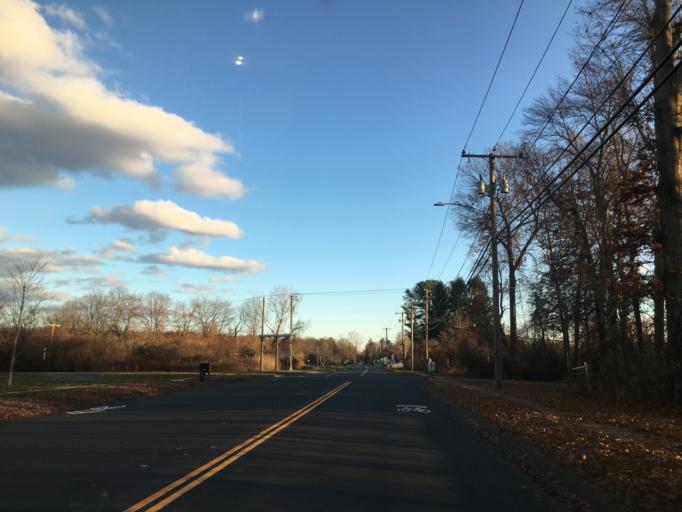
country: US
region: Connecticut
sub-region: Hartford County
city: Southwood Acres
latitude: 41.9636
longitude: -72.5797
